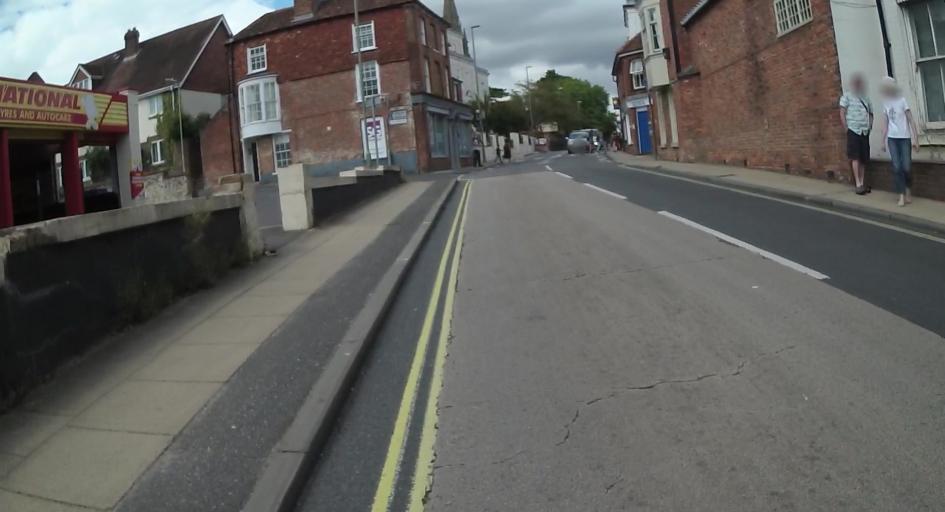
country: GB
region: England
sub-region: Hampshire
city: Winchester
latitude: 51.0597
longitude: -1.3186
